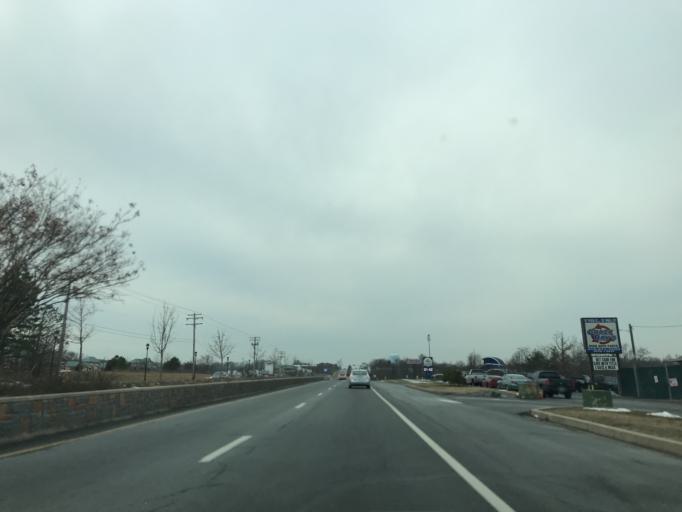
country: US
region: Maryland
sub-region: Harford County
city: Edgewood
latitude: 39.4344
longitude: -76.3211
